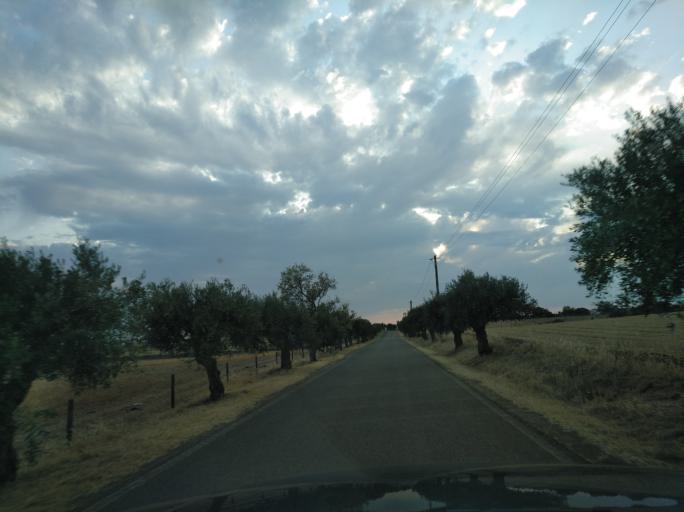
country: PT
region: Portalegre
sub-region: Campo Maior
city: Campo Maior
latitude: 39.0167
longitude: -7.0432
